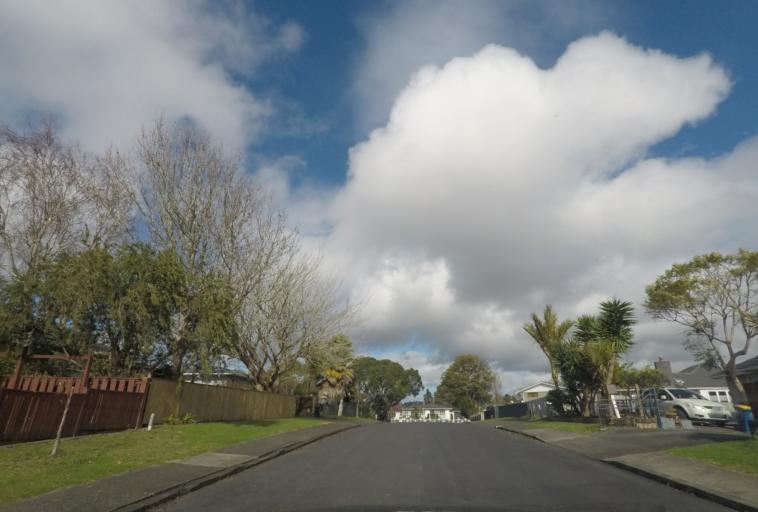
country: NZ
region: Auckland
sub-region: Auckland
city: Rosebank
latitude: -36.8952
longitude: 174.6624
